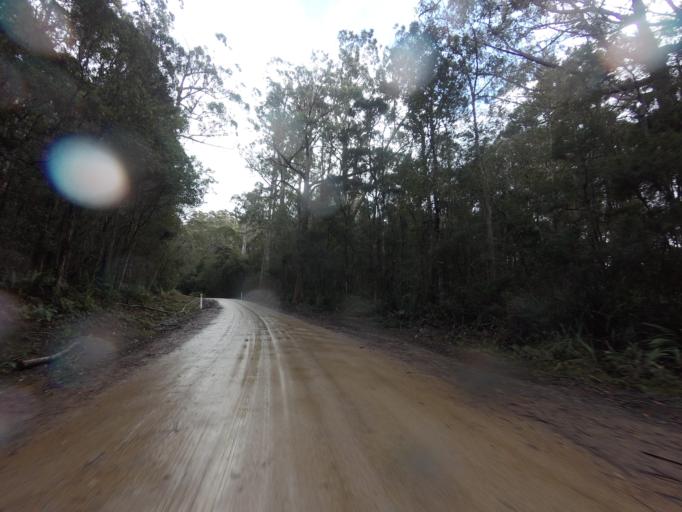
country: AU
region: Tasmania
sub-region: Huon Valley
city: Geeveston
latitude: -43.5759
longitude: 146.8884
